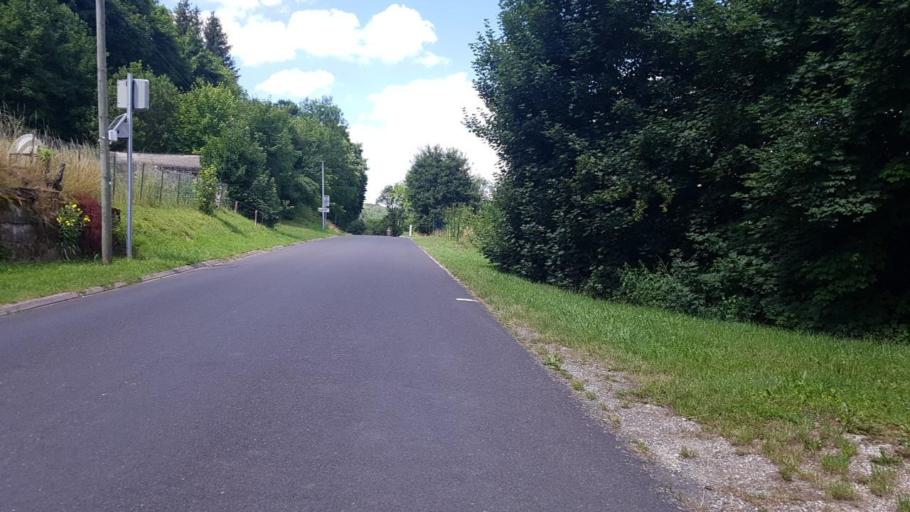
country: FR
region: Lorraine
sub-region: Departement de la Meuse
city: Gondrecourt-le-Chateau
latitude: 48.6307
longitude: 5.4650
